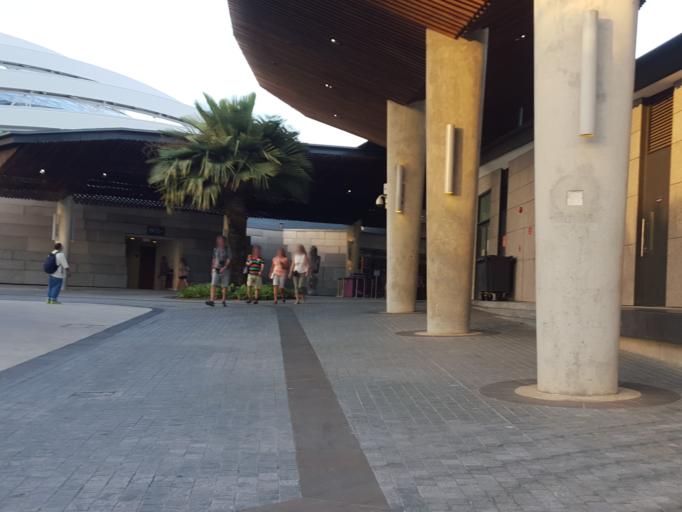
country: SG
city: Singapore
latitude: 1.2837
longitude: 103.8648
